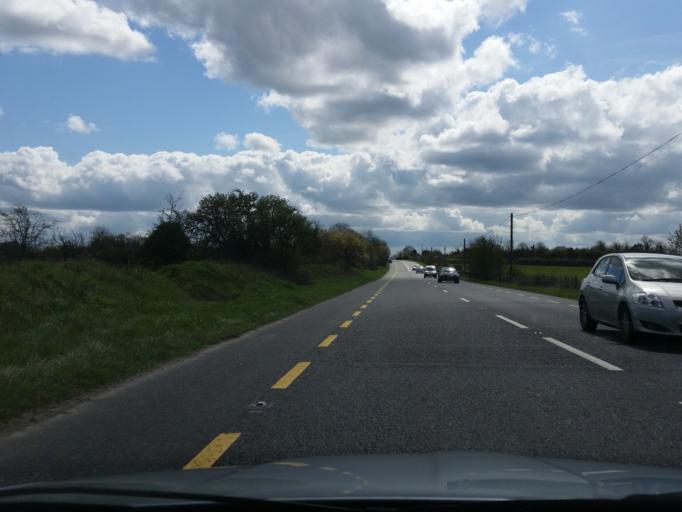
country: IE
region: Leinster
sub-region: An Mhi
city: Slane
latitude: 53.6809
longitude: -6.5398
